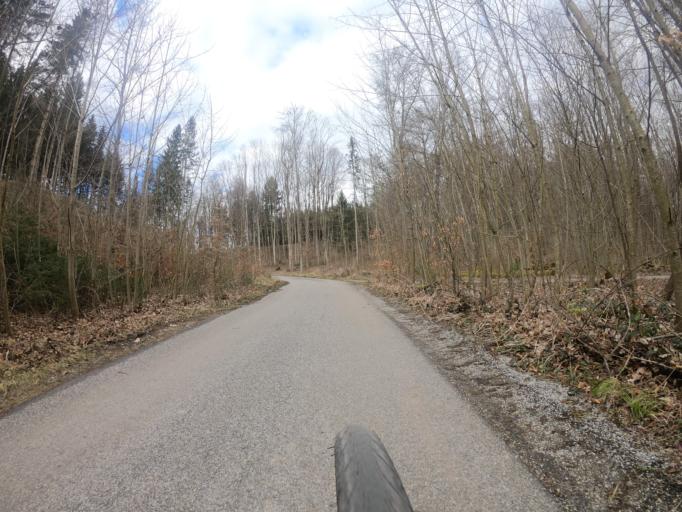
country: DE
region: Bavaria
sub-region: Upper Bavaria
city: Schongeising
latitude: 48.1690
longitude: 11.2017
